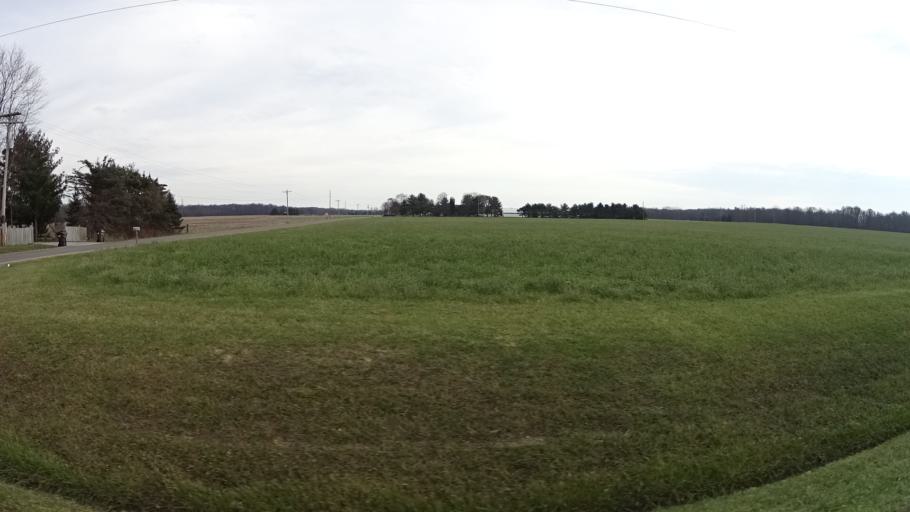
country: US
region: Ohio
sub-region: Lorain County
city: Wellington
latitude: 41.1540
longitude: -82.1695
